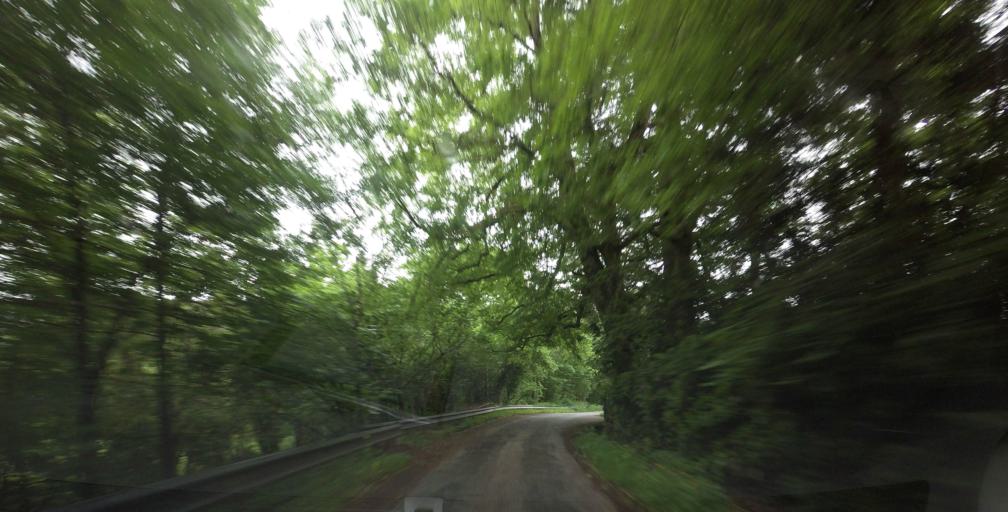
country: GB
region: Scotland
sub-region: Argyll and Bute
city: Oban
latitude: 56.7097
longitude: -5.5630
